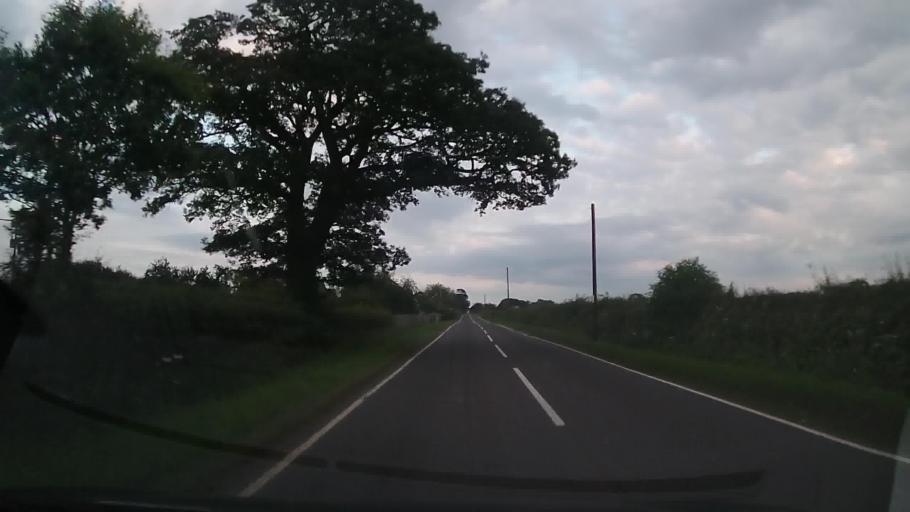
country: GB
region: England
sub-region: Shropshire
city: Petton
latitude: 52.8087
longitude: -2.8056
